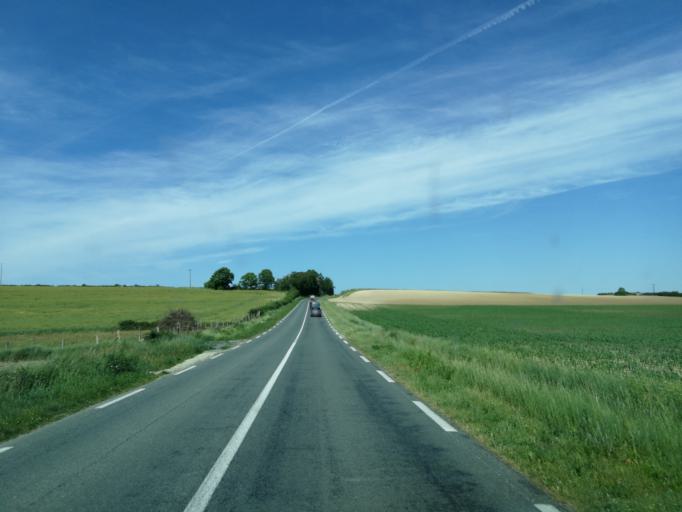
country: FR
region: Poitou-Charentes
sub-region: Departement de la Vienne
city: Loudun
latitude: 47.0253
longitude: 0.1081
